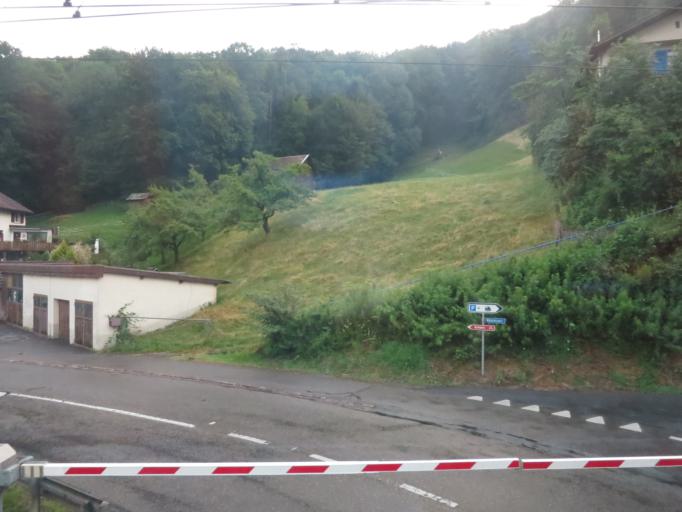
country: CH
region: Glarus
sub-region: Glarus
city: Niederurnen
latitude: 47.1391
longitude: 9.0545
